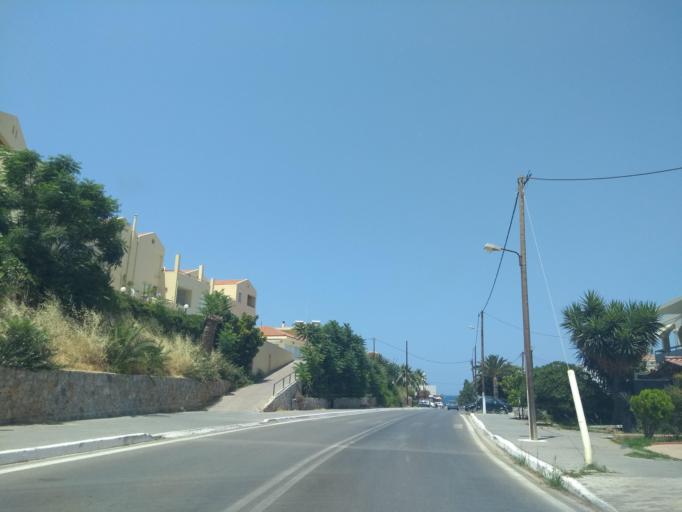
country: GR
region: Crete
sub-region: Nomos Chanias
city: Daratsos
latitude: 35.5083
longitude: 23.9882
